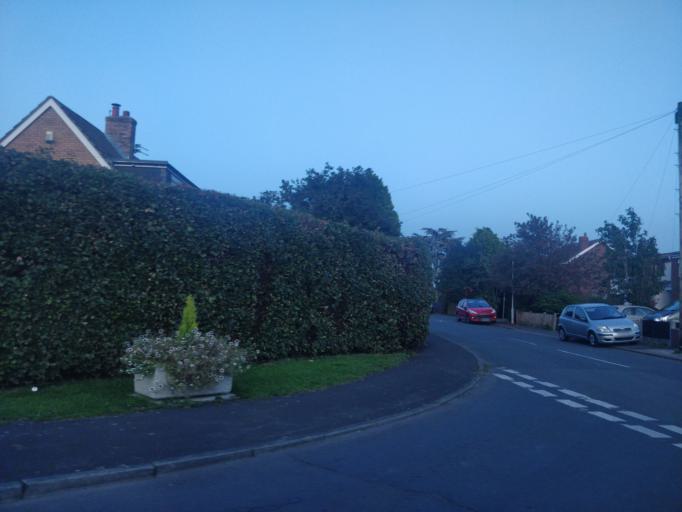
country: GB
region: England
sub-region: Lancashire
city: Tarleton
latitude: 53.6985
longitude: -2.8012
